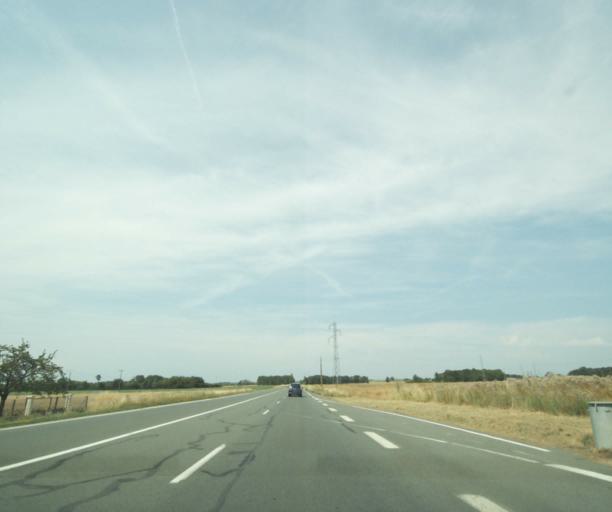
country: FR
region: Centre
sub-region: Departement d'Indre-et-Loire
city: Sorigny
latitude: 47.2084
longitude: 0.6754
